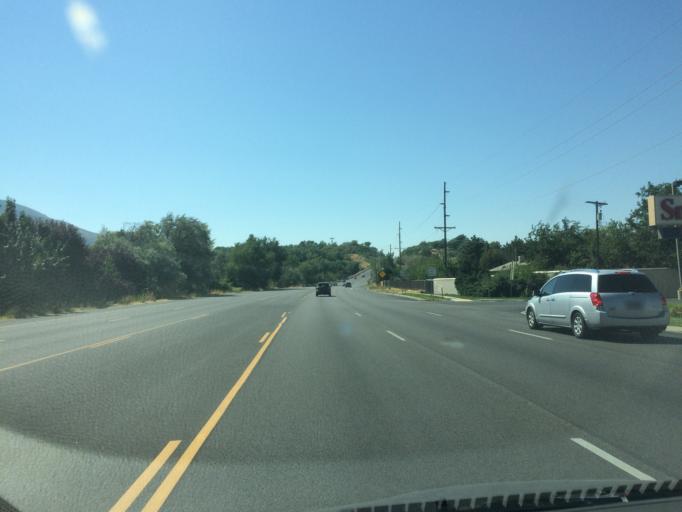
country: US
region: Utah
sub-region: Weber County
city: Ogden
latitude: 41.2405
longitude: -111.9455
